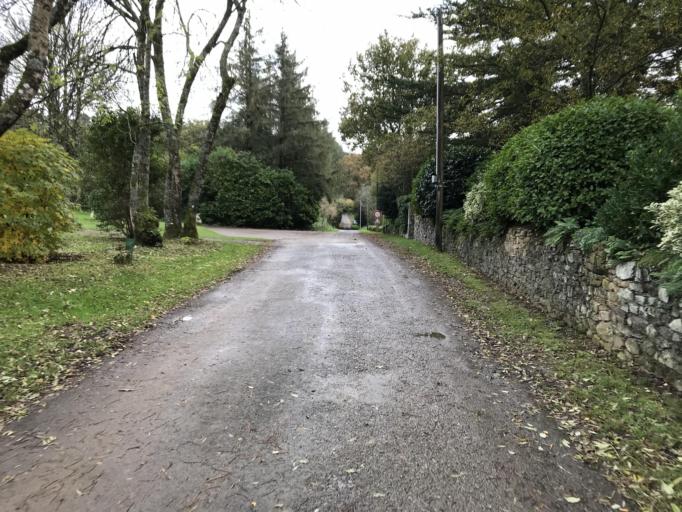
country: FR
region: Brittany
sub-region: Departement du Finistere
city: Irvillac
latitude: 48.3447
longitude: -4.2110
